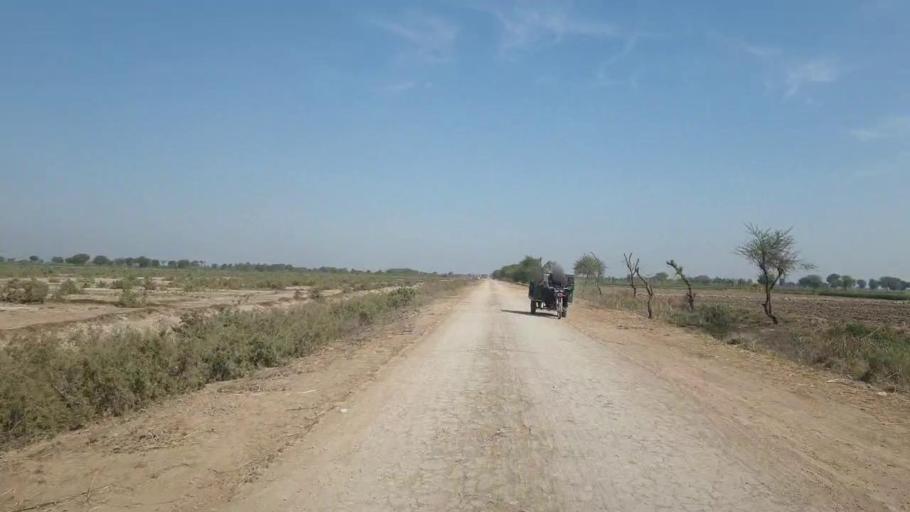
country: PK
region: Sindh
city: Samaro
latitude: 25.3285
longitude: 69.2433
